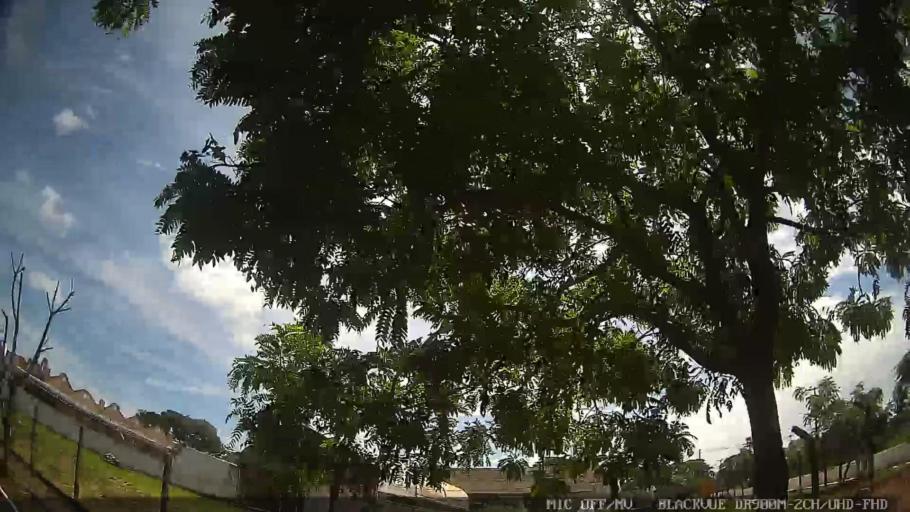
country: BR
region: Sao Paulo
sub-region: Jaguariuna
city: Jaguariuna
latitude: -22.6142
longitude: -47.0607
